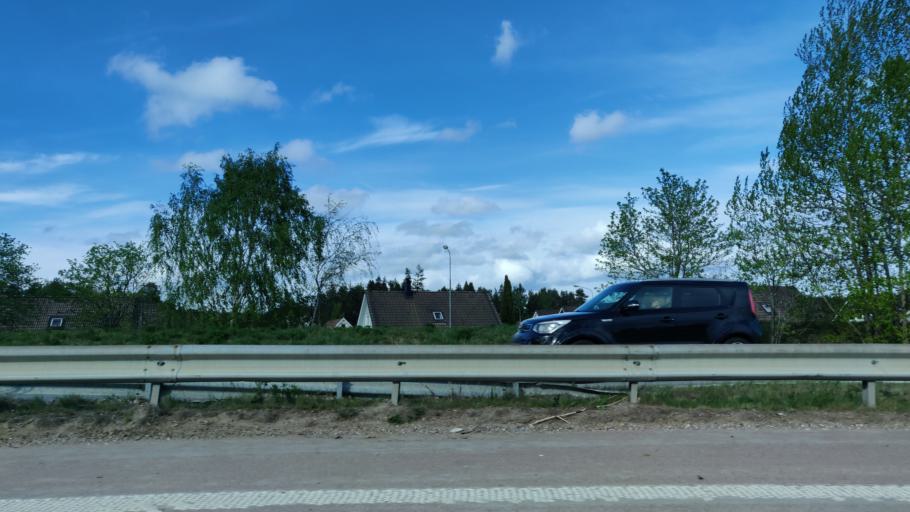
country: SE
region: Vaermland
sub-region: Karlstads Kommun
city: Karlstad
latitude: 59.3800
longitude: 13.4430
